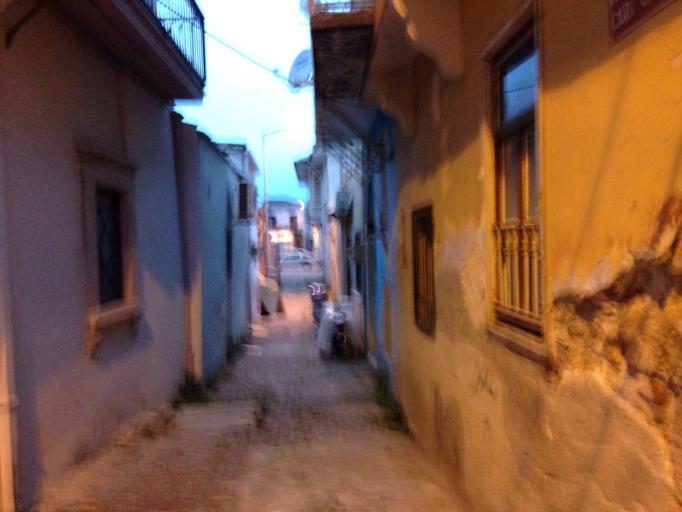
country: TR
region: Balikesir
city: Ayvalik
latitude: 39.3209
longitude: 26.6937
